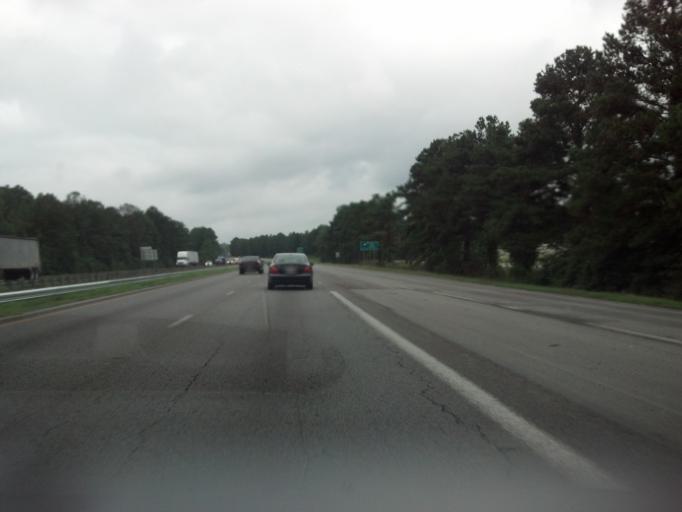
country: US
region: North Carolina
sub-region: Nash County
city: Rocky Mount
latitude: 35.9614
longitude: -77.7946
